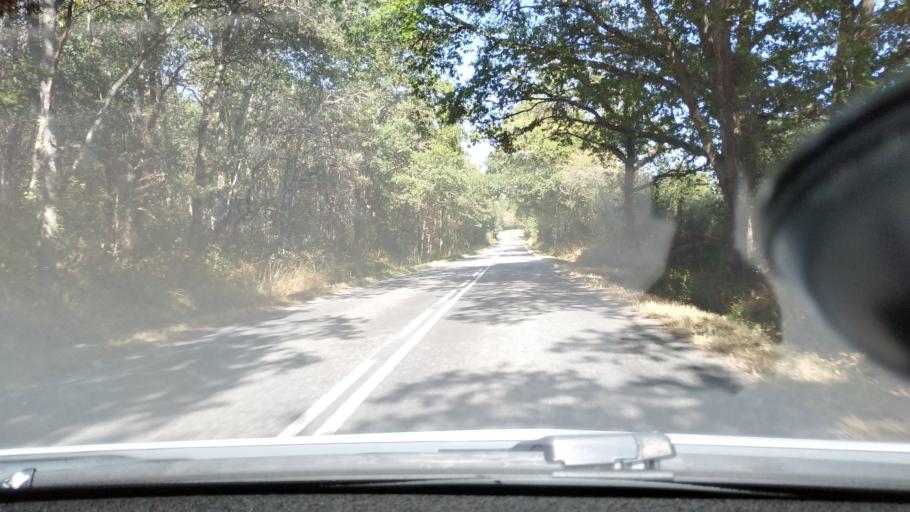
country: FR
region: Centre
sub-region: Departement du Loiret
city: Coullons
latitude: 47.6359
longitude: 2.5177
